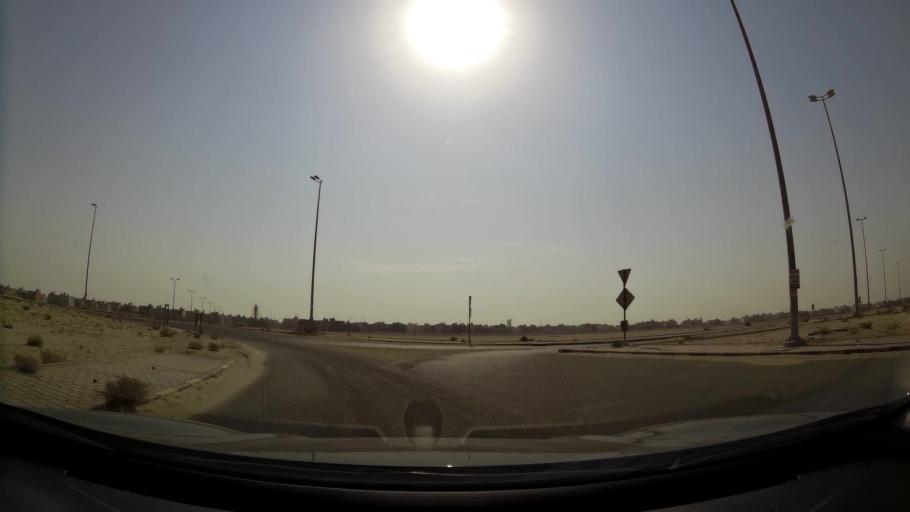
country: KW
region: Al Ahmadi
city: Al Wafrah
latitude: 28.7916
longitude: 48.0762
